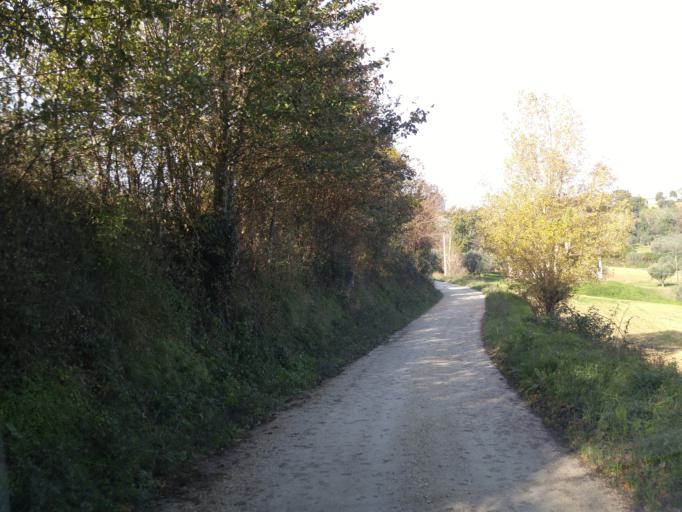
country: IT
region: The Marches
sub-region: Provincia di Pesaro e Urbino
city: Saltara
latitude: 43.7596
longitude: 12.9016
